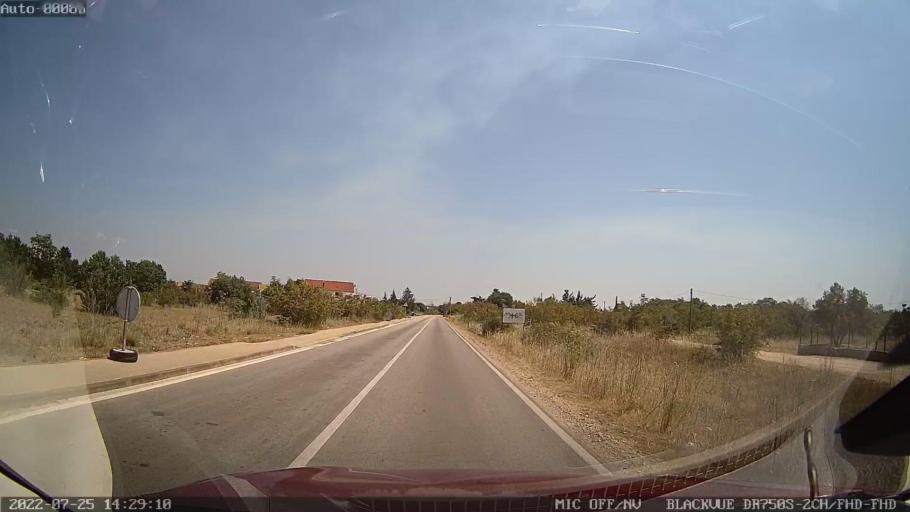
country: HR
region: Zadarska
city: Policnik
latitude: 44.1217
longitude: 15.3541
